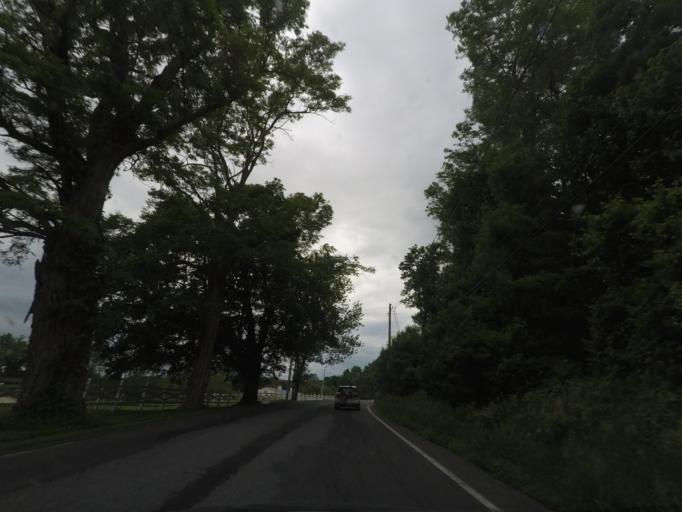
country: US
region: New York
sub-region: Dutchess County
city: Pine Plains
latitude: 41.9766
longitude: -73.5802
